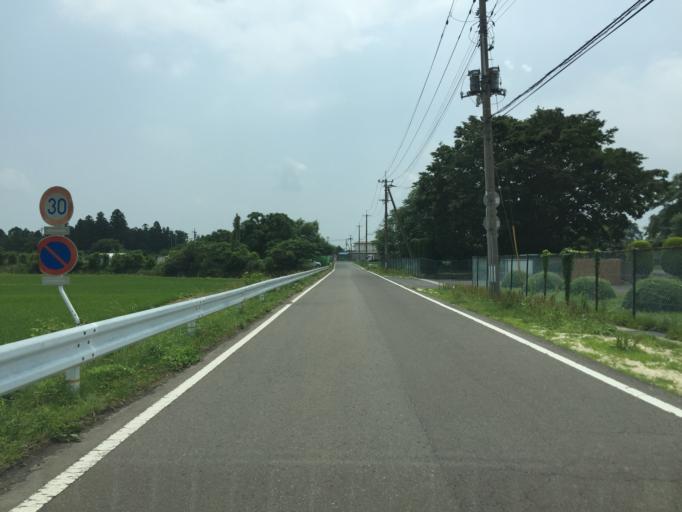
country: JP
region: Fukushima
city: Fukushima-shi
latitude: 37.7626
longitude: 140.3746
